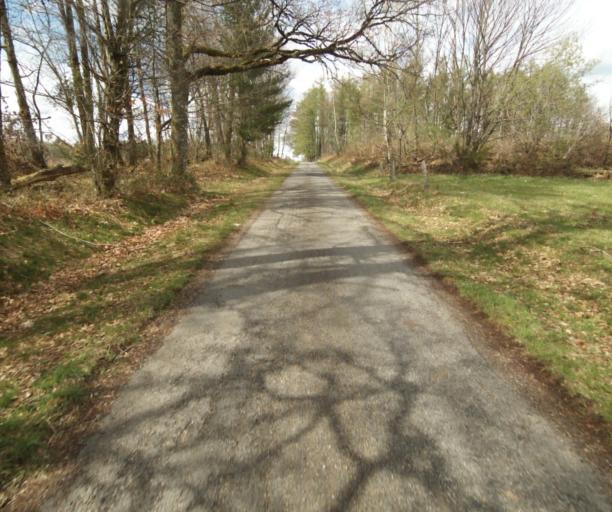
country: FR
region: Limousin
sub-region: Departement de la Correze
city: Argentat
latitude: 45.1894
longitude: 1.9137
